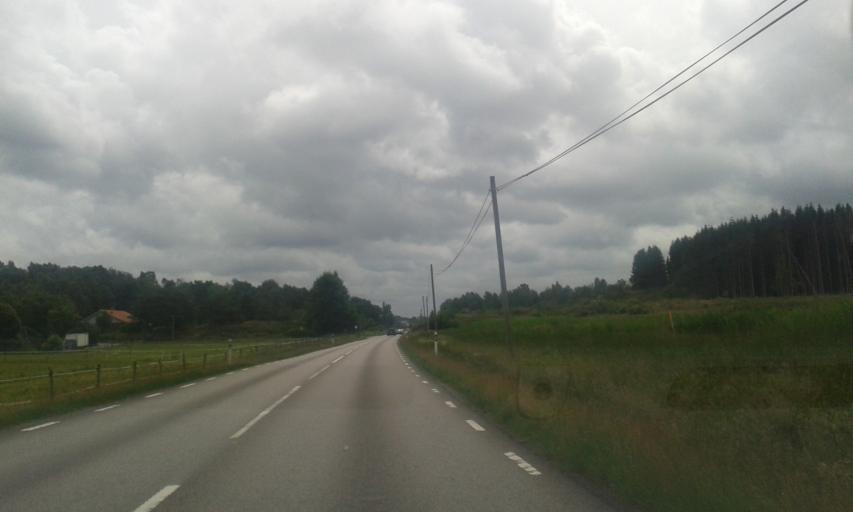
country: SE
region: Vaestra Goetaland
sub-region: Kungalvs Kommun
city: Kode
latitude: 57.8903
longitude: 11.8836
